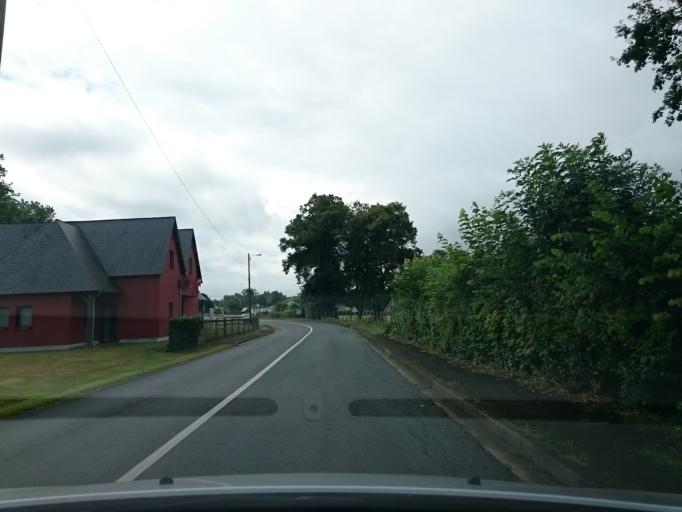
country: FR
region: Lower Normandy
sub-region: Departement du Calvados
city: Beuvillers
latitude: 49.1086
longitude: 0.2895
